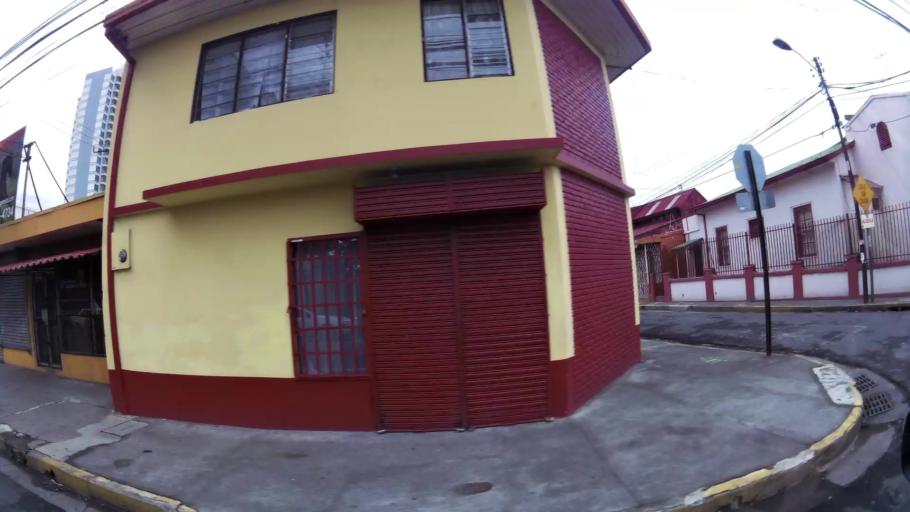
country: CR
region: San Jose
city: San Jose
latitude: 9.9362
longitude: -84.0895
